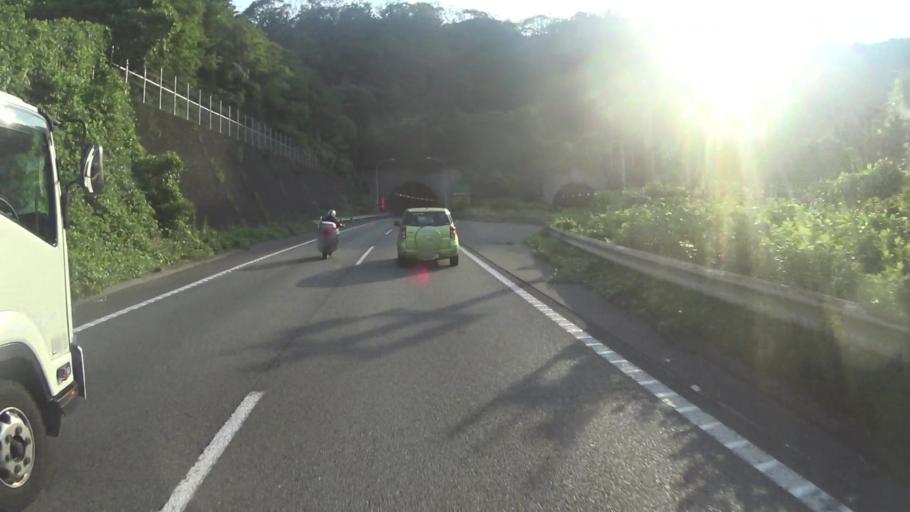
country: JP
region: Kyoto
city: Uji
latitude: 34.9164
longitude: 135.8688
